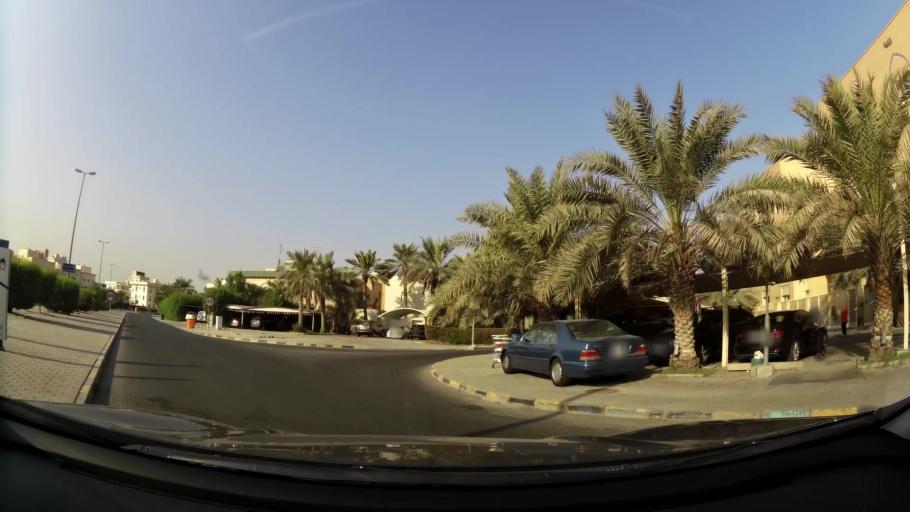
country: KW
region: Al Asimah
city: Ad Dasmah
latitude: 29.3672
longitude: 48.0068
